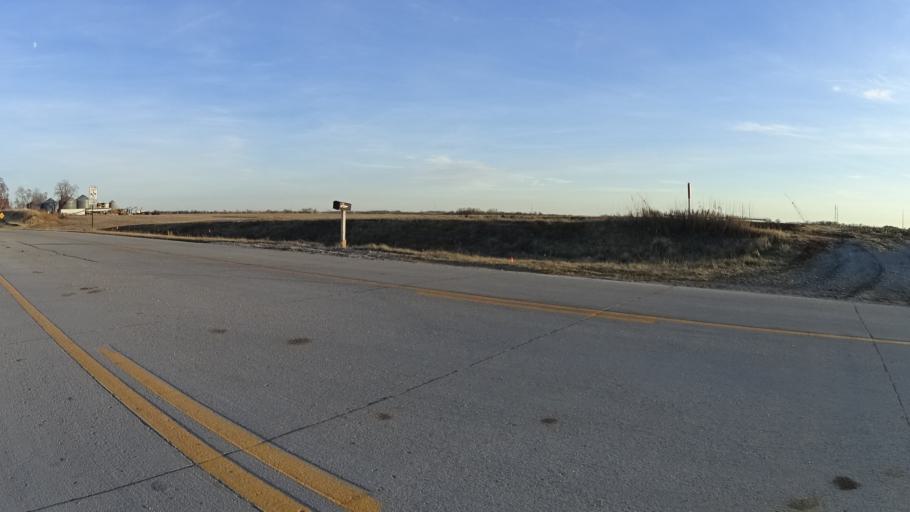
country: US
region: Nebraska
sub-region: Sarpy County
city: Springfield
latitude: 41.1326
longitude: -96.1351
